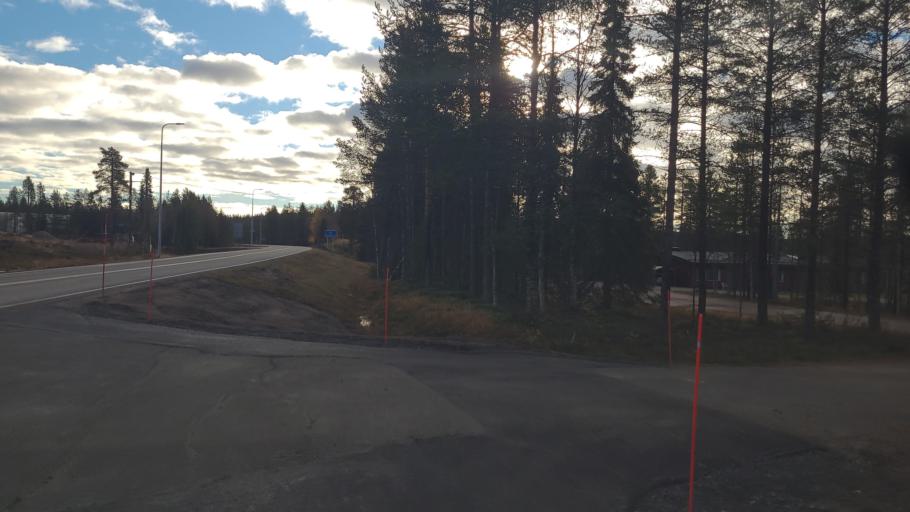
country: FI
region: Lapland
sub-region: Itae-Lappi
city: Posio
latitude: 66.1062
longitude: 28.1808
